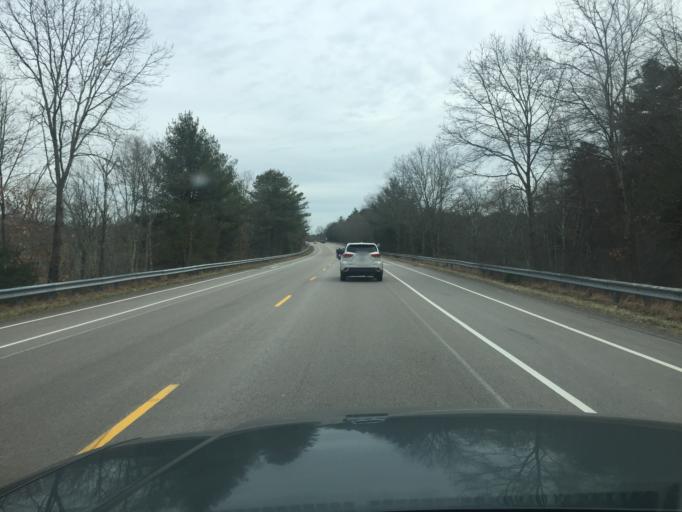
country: US
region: Massachusetts
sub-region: Norfolk County
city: Medfield
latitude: 42.1981
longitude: -71.3328
